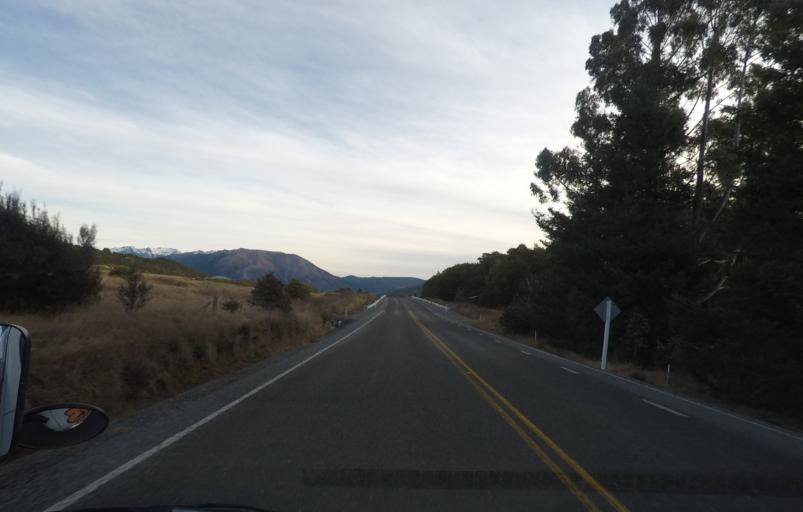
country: NZ
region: Tasman
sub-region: Tasman District
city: Wakefield
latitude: -41.7858
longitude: 172.8922
